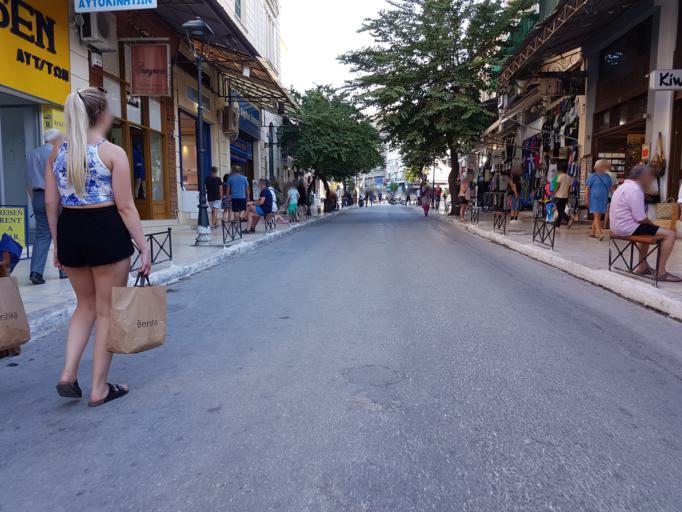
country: GR
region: Crete
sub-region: Nomos Chanias
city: Chania
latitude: 35.5152
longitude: 24.0170
